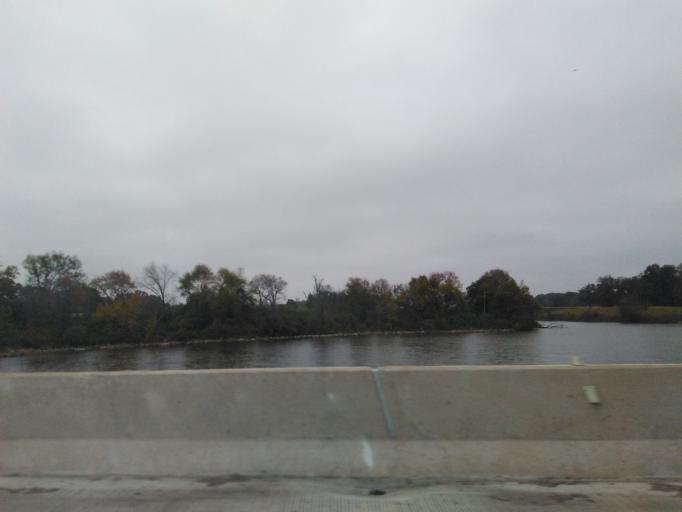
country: US
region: Illinois
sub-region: Madison County
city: Highland
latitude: 38.7863
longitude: -89.6967
